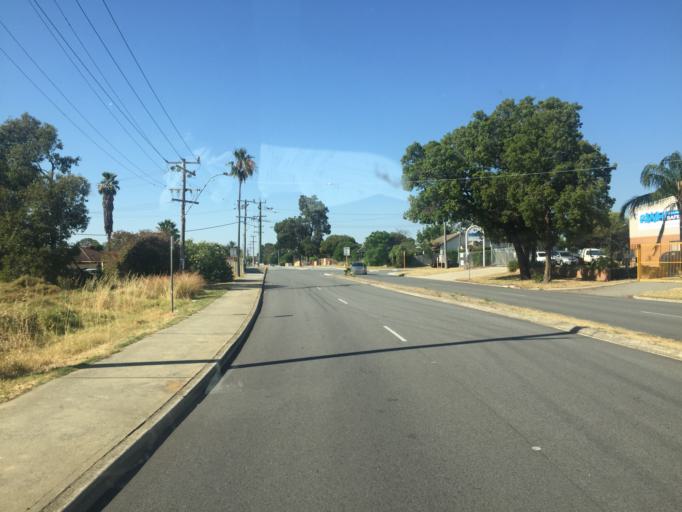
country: AU
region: Western Australia
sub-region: Gosnells
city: Maddington
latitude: -32.0408
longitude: 115.9819
